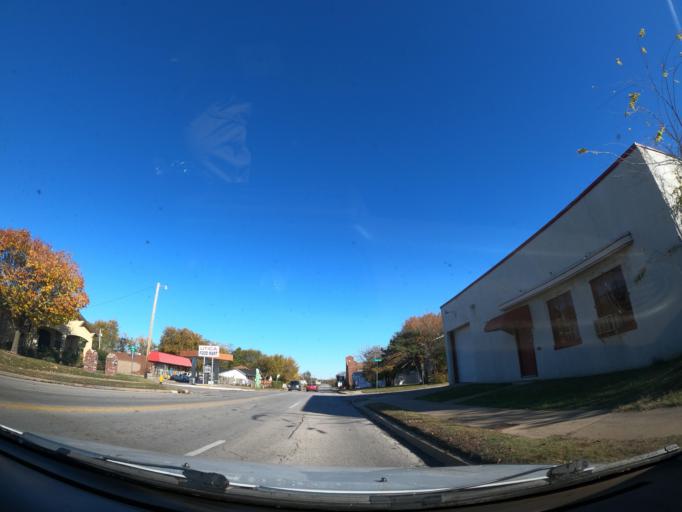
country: US
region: Oklahoma
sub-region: Tulsa County
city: Tulsa
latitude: 36.1676
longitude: -95.9671
